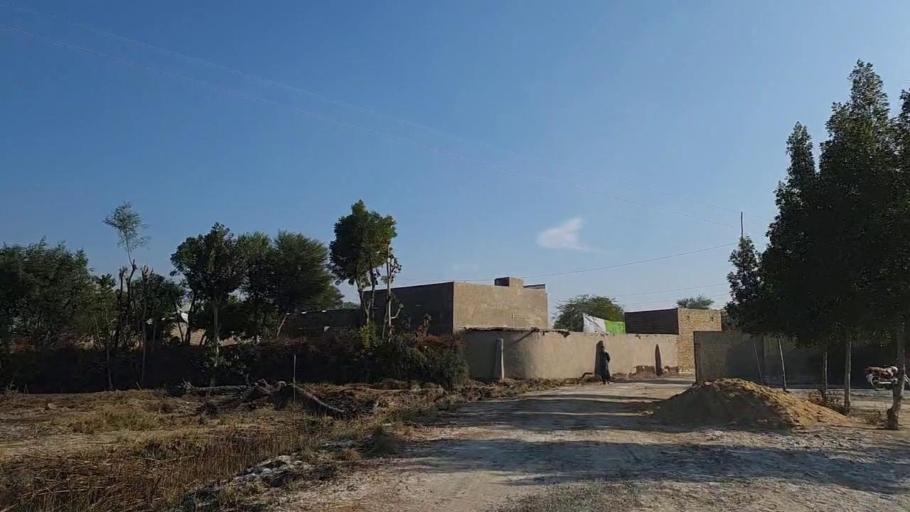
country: PK
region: Sindh
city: Bandhi
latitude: 26.5725
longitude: 68.3113
